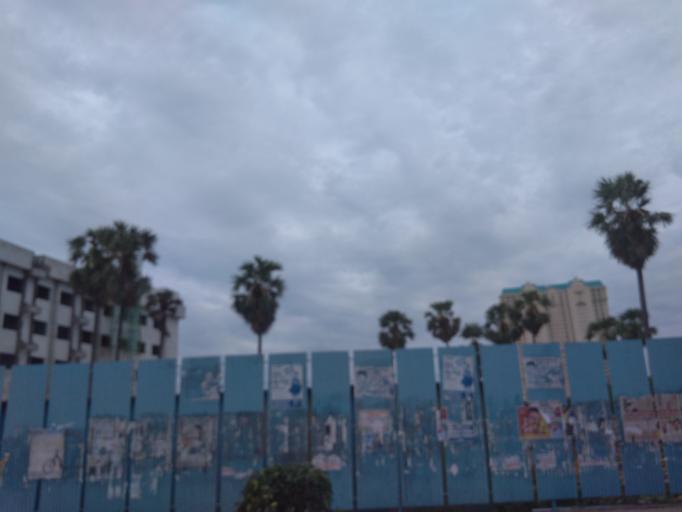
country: IN
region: Tamil Nadu
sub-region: Kancheepuram
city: Injambakkam
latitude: 12.8398
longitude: 80.2277
